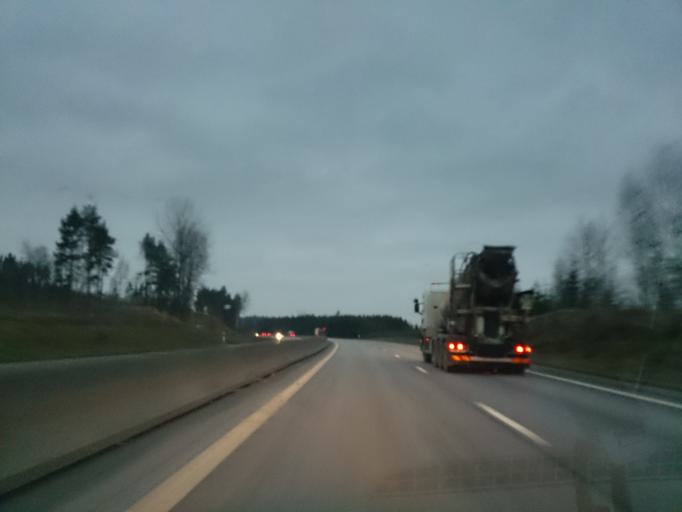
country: SE
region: OEstergoetland
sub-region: Norrkopings Kommun
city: Kimstad
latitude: 58.5234
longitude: 16.0072
